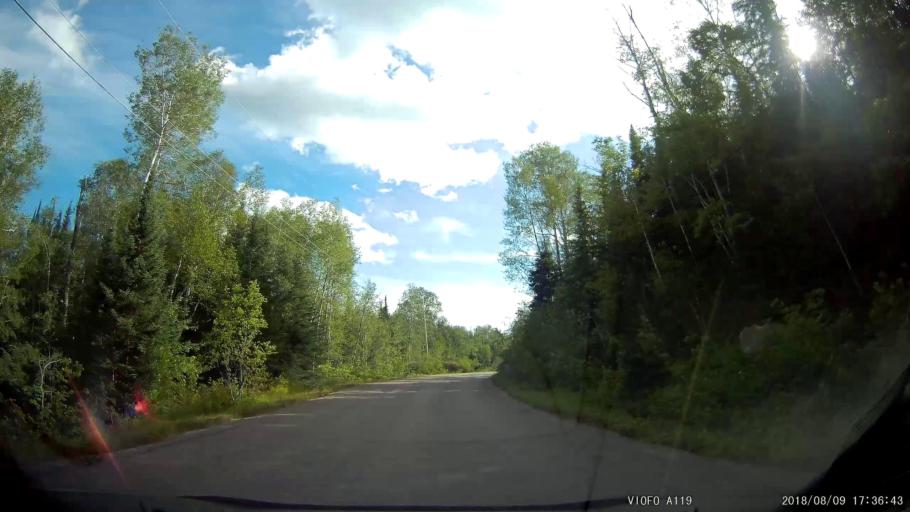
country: CA
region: Ontario
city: Rayside-Balfour
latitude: 46.6148
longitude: -81.4687
